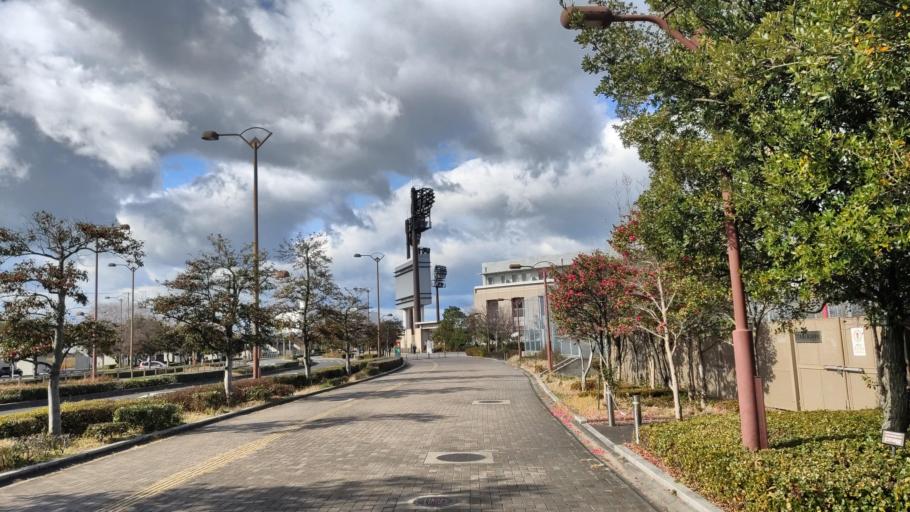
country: JP
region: Ehime
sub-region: Shikoku-chuo Shi
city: Matsuyama
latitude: 33.8076
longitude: 132.7443
